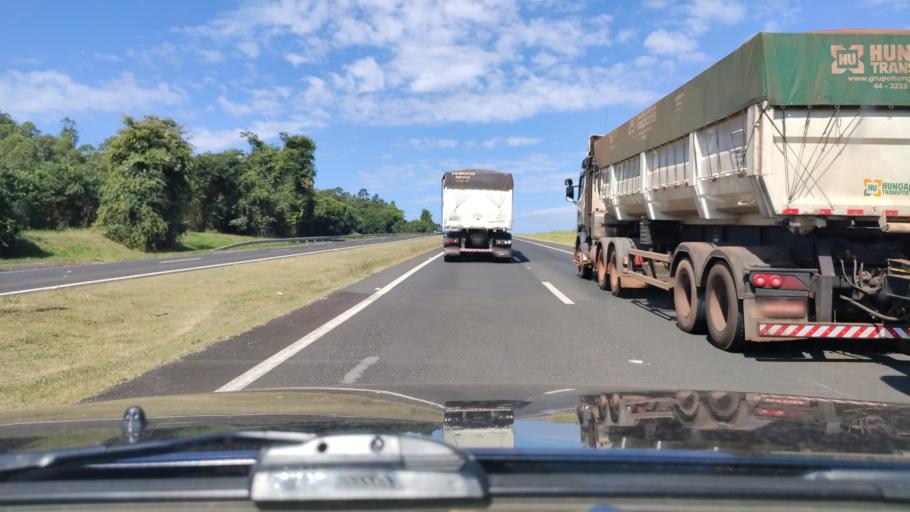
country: BR
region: Sao Paulo
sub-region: Rancharia
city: Rancharia
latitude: -22.4250
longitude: -51.0253
